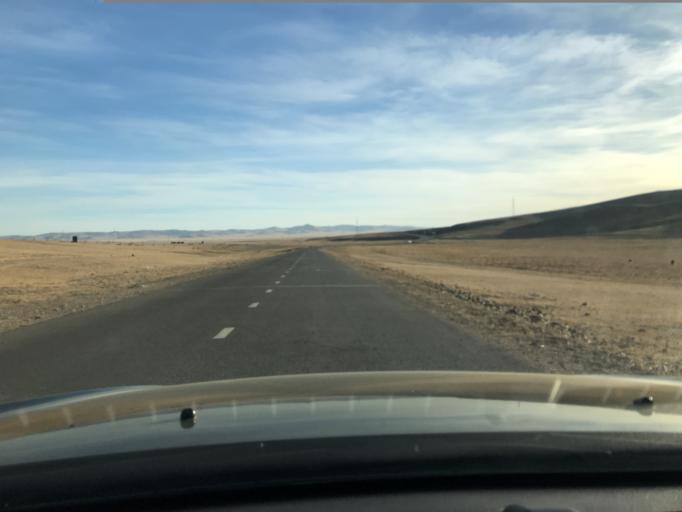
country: MN
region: Central Aimak
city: Dzuunmod
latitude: 47.8004
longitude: 107.3238
